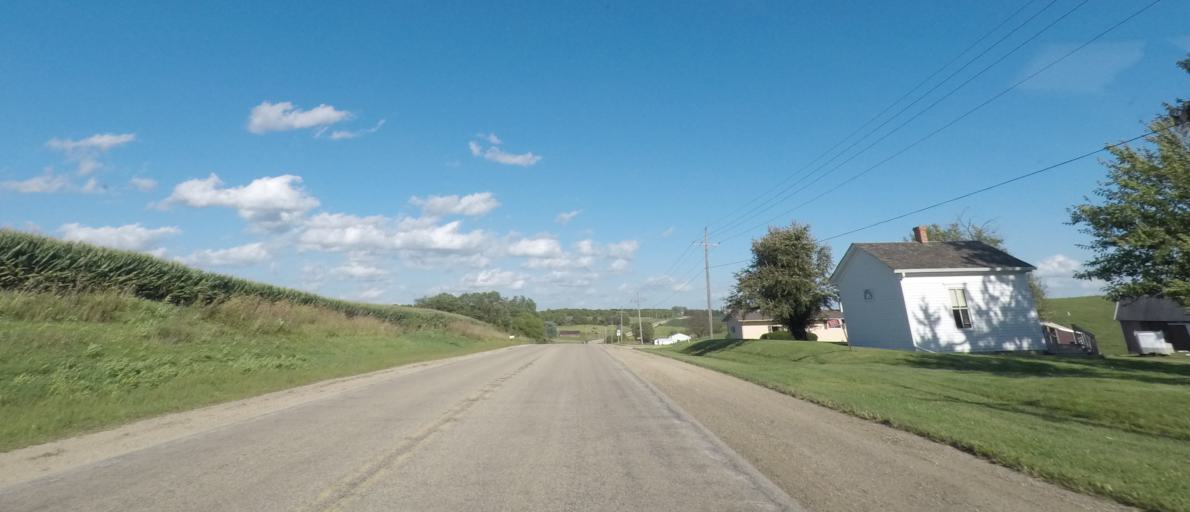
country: US
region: Wisconsin
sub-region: Iowa County
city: Dodgeville
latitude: 42.9816
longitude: -90.0830
